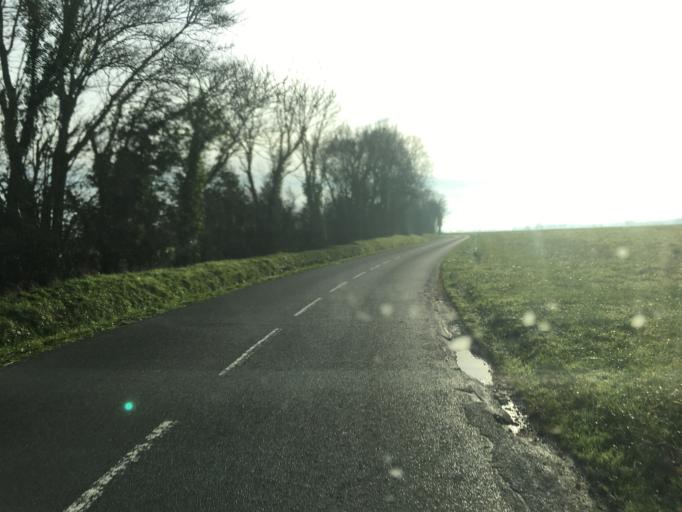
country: FR
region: Lower Normandy
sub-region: Departement du Calvados
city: Dozule
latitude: 49.1968
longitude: -0.0637
